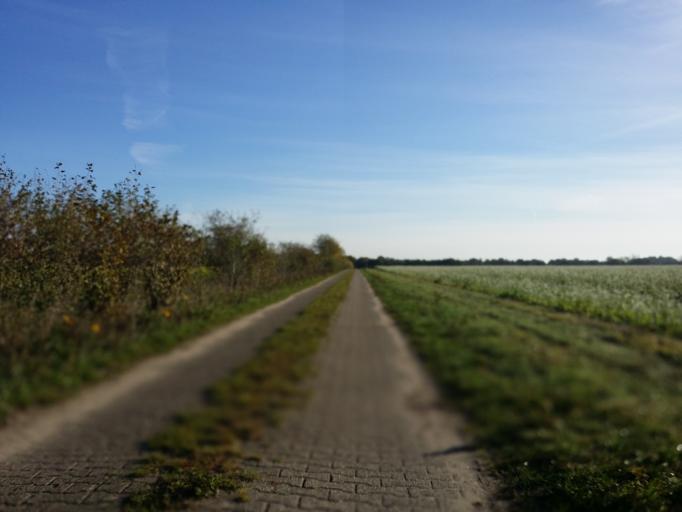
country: DE
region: Lower Saxony
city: Tarmstedt
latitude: 53.2037
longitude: 9.0700
